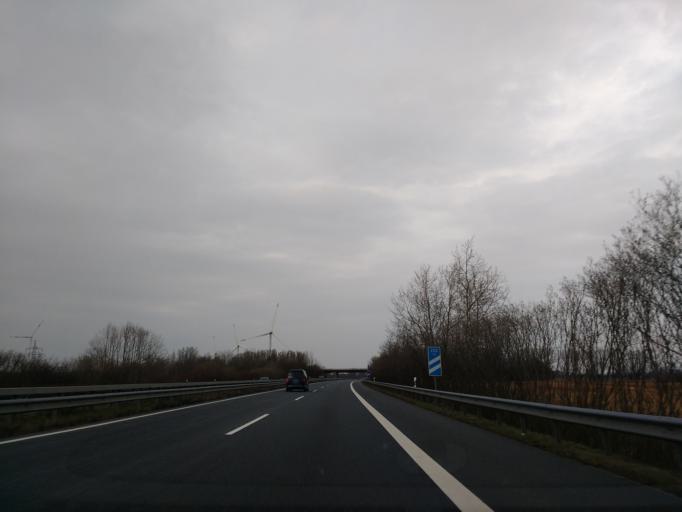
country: DE
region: Lower Saxony
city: Cuxhaven
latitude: 53.8150
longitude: 8.7084
